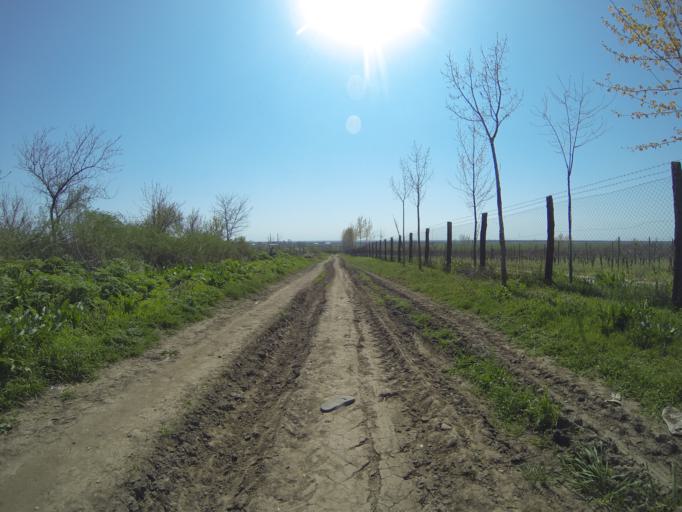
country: RO
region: Dolj
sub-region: Comuna Segarcea
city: Segarcea
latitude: 44.1017
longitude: 23.7257
